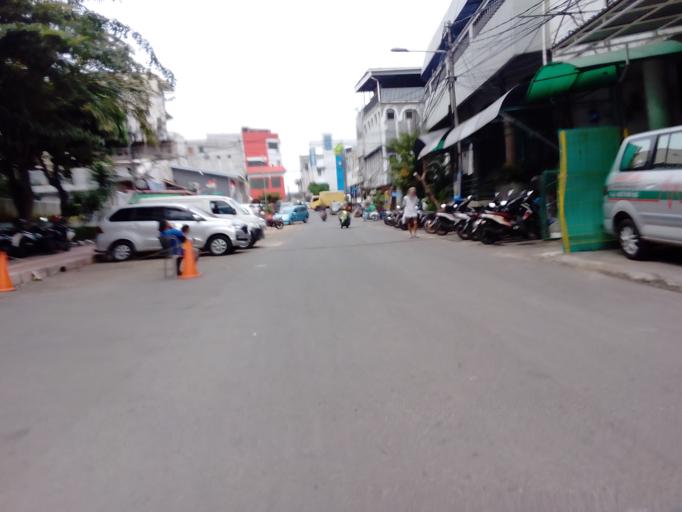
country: ID
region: Jakarta Raya
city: Jakarta
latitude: -6.1545
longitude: 106.8170
